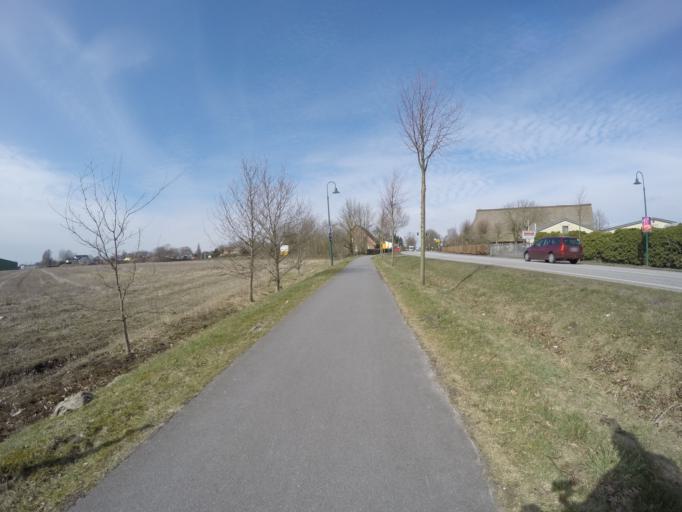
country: DE
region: Schleswig-Holstein
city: Bilsen
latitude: 53.7688
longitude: 9.8764
